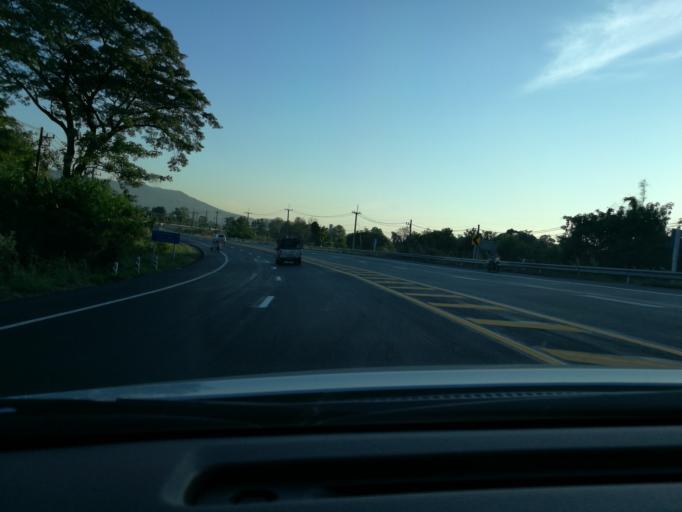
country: TH
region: Phitsanulok
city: Wang Thong
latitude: 16.8602
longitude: 100.4803
